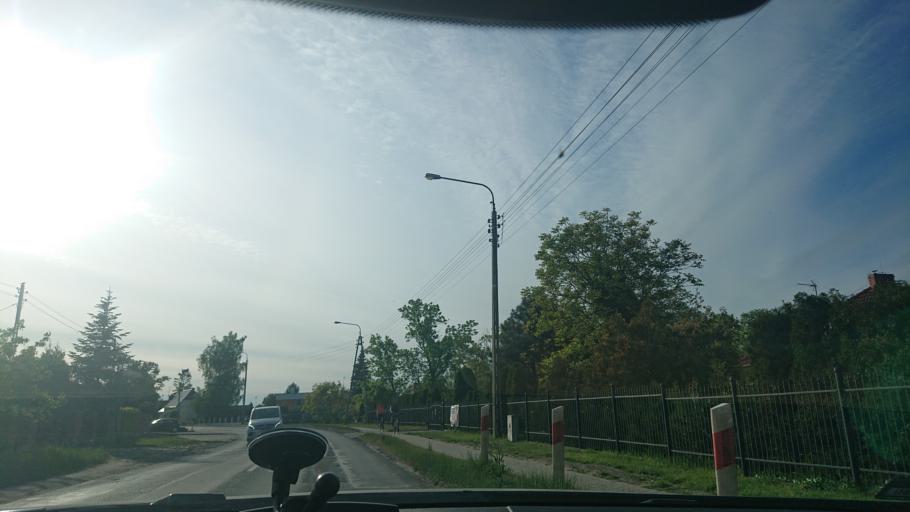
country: PL
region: Greater Poland Voivodeship
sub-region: Powiat gnieznienski
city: Gniezno
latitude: 52.5431
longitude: 17.5745
